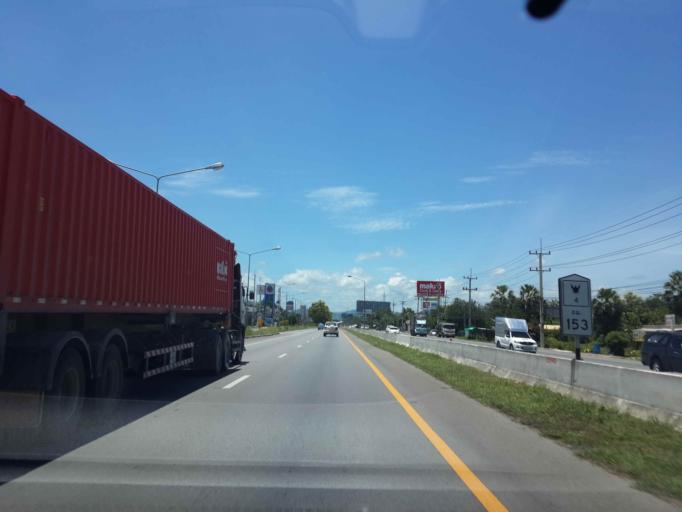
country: TH
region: Phetchaburi
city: Phetchaburi
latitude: 13.1222
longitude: 99.8902
